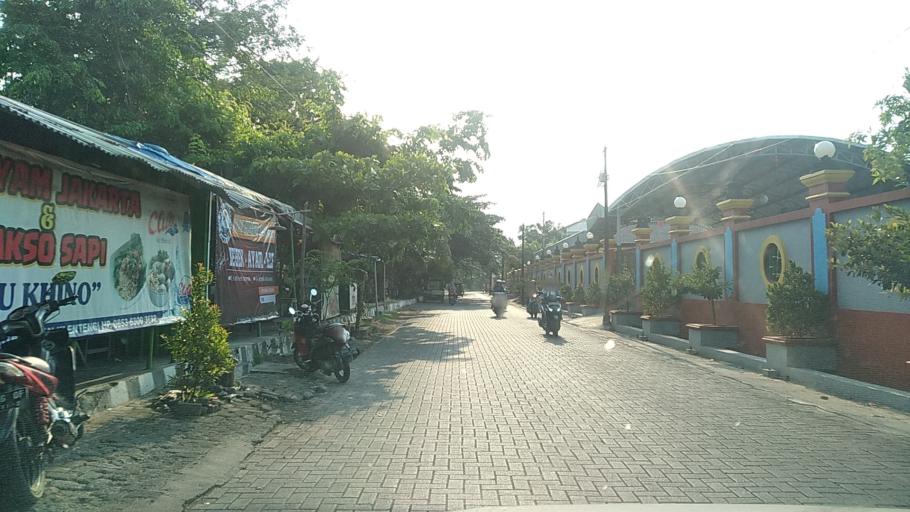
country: ID
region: Central Java
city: Semarang
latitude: -6.9652
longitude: 110.4051
